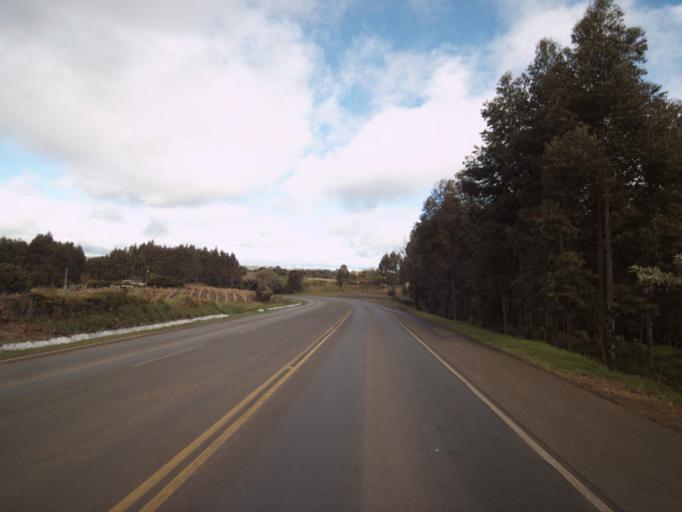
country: BR
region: Santa Catarina
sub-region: Concordia
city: Concordia
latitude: -27.1102
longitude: -51.9078
